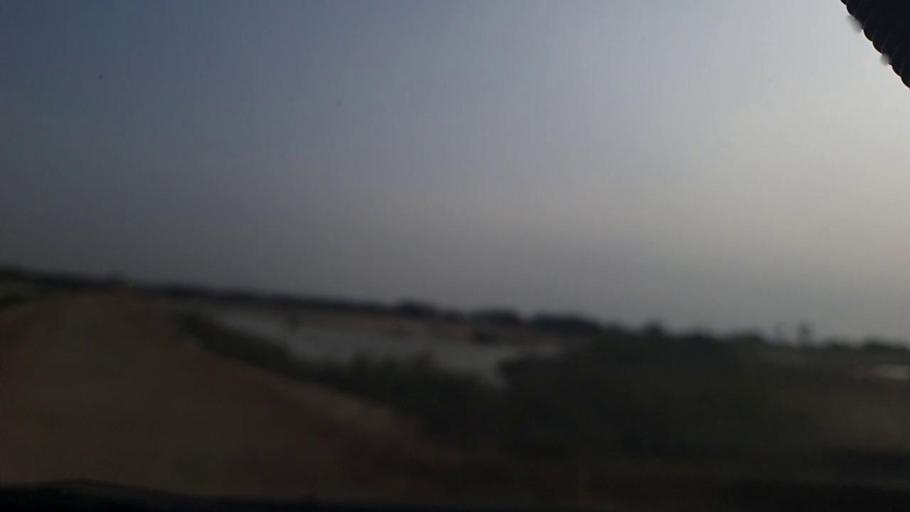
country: PK
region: Sindh
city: Thatta
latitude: 24.7246
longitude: 67.9021
